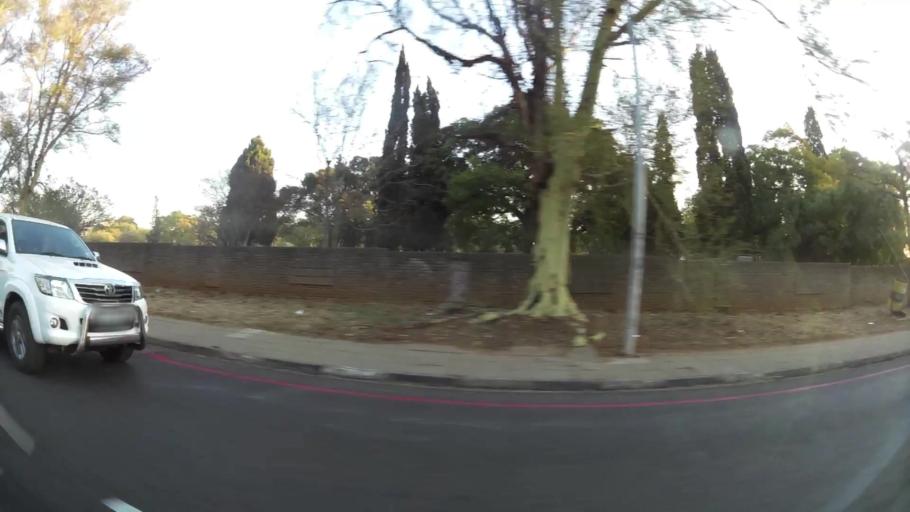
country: ZA
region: North-West
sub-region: Bojanala Platinum District Municipality
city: Rustenburg
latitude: -25.6744
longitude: 27.2447
